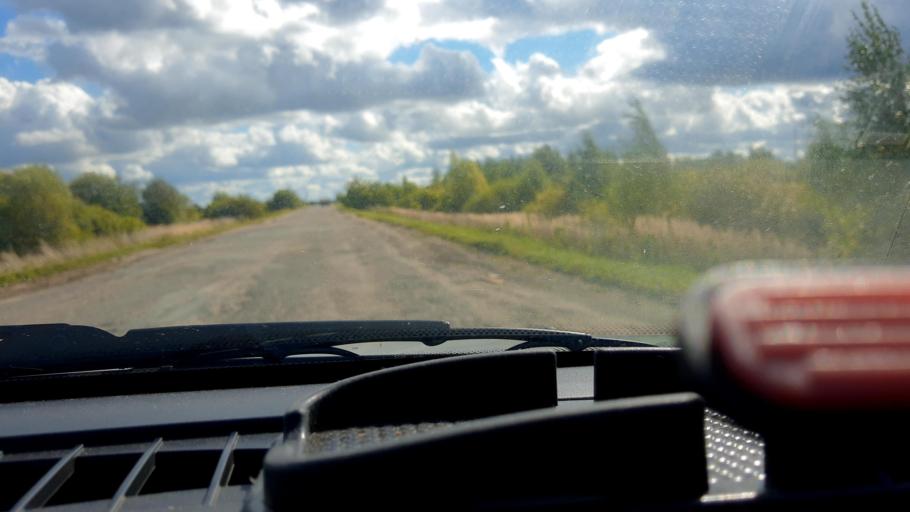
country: RU
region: Nizjnij Novgorod
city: Sharanga
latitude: 56.9403
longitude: 46.6475
